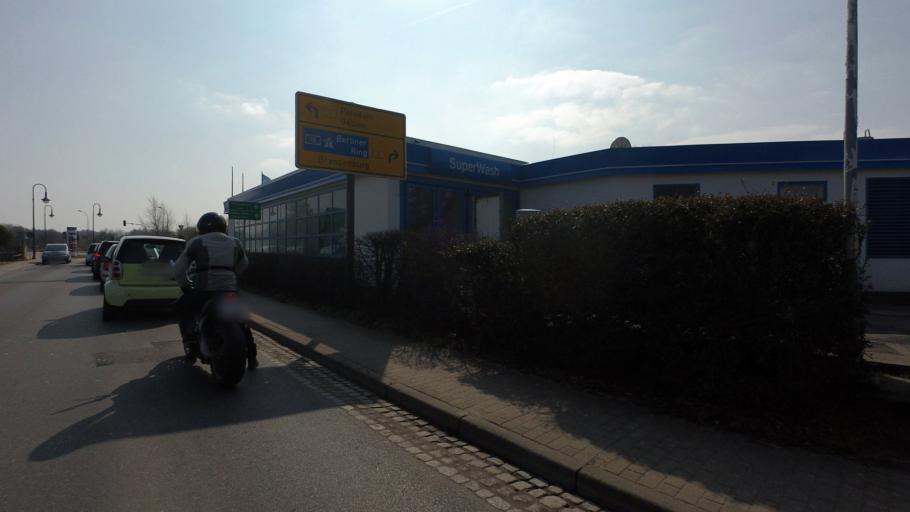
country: DE
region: Brandenburg
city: Werder
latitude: 52.3648
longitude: 12.9408
